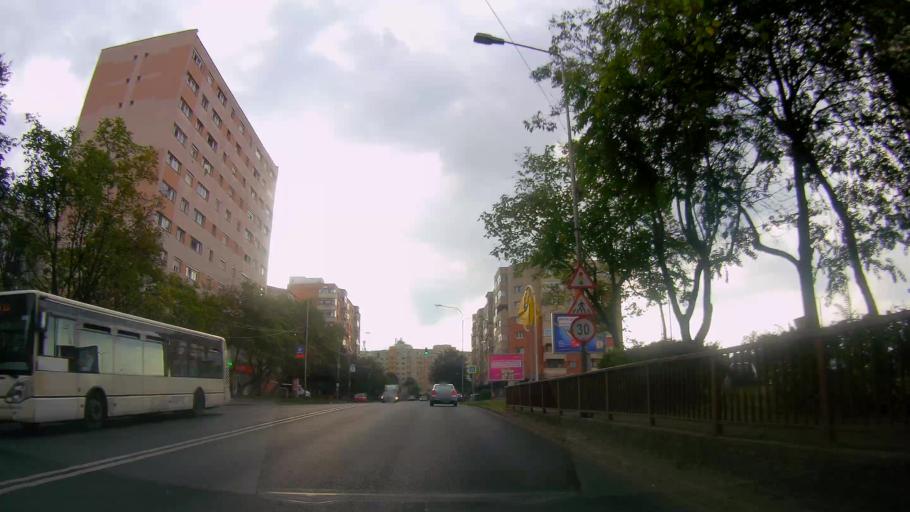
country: RO
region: Satu Mare
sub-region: Municipiul Satu Mare
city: Satu Mare
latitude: 47.7809
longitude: 22.8800
